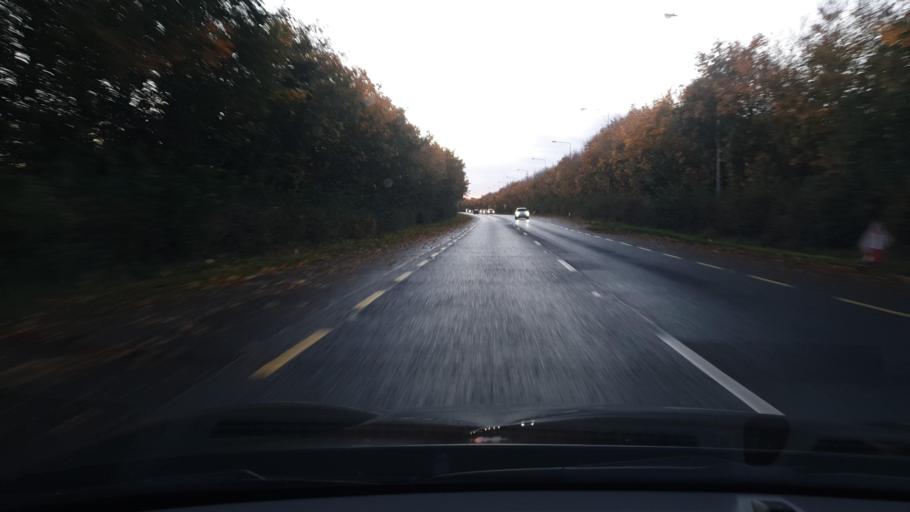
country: IE
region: Leinster
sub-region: Lu
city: Drogheda
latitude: 53.7301
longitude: -6.3784
